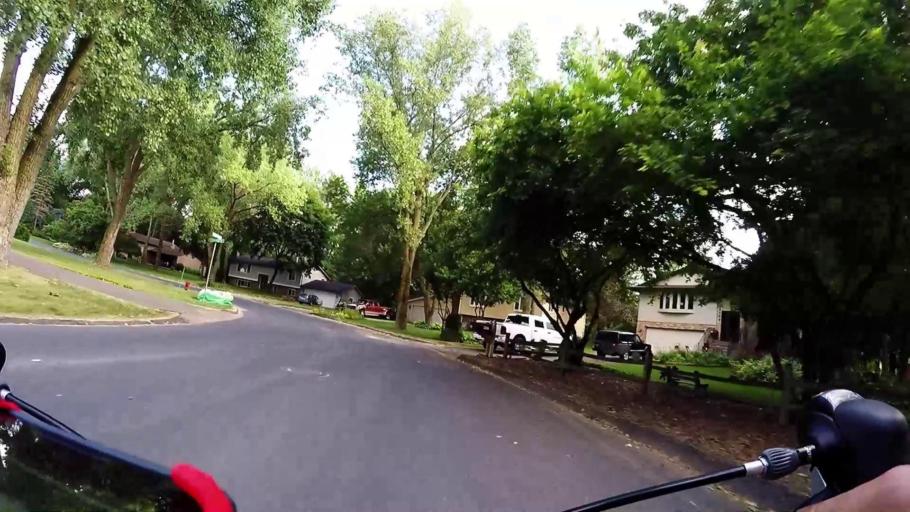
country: US
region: Minnesota
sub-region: Hennepin County
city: Eden Prairie
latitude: 44.8861
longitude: -93.4793
